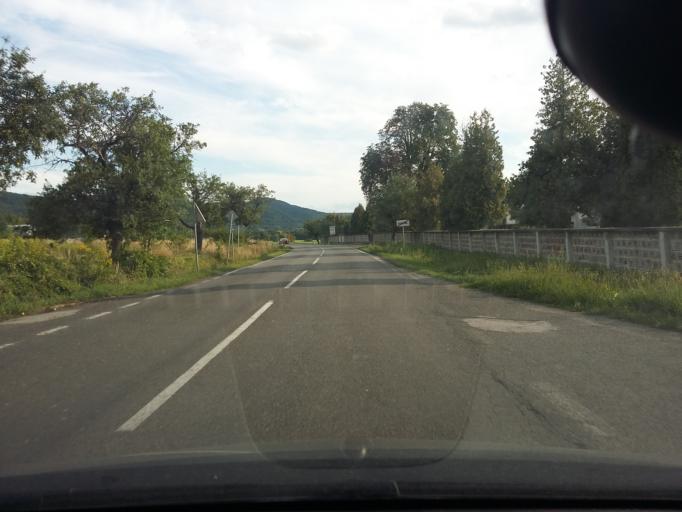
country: SK
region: Bratislavsky
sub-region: Okres Malacky
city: Malacky
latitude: 48.4034
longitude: 17.1549
